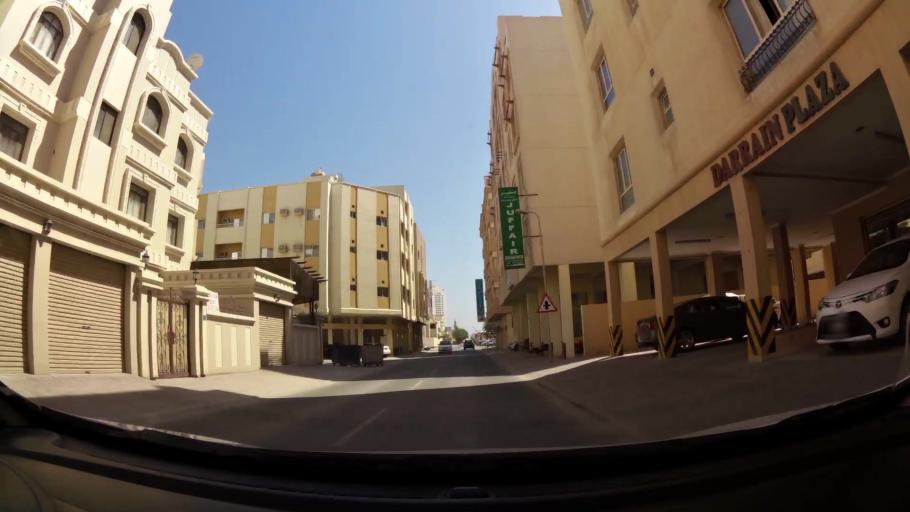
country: BH
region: Manama
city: Manama
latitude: 26.2121
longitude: 50.6115
